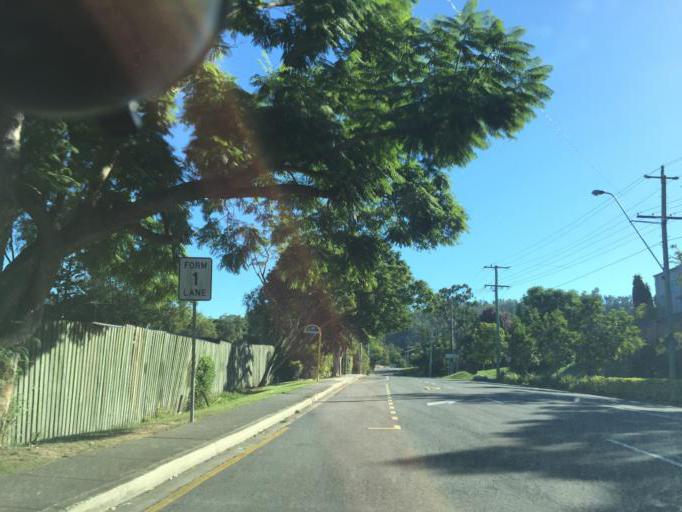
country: AU
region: Queensland
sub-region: Moreton Bay
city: Ferny Hills
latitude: -27.4356
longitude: 152.9432
